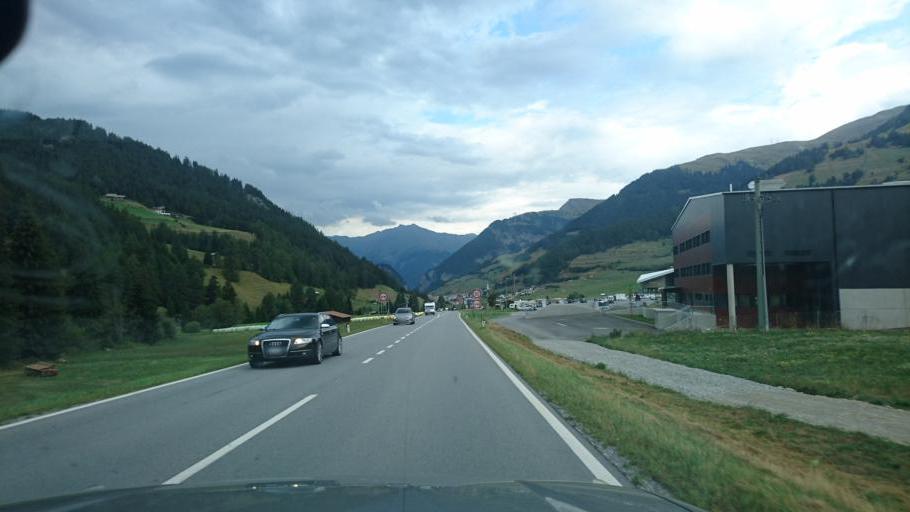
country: AT
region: Tyrol
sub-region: Politischer Bezirk Landeck
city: Nauders
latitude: 46.8727
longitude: 10.5078
